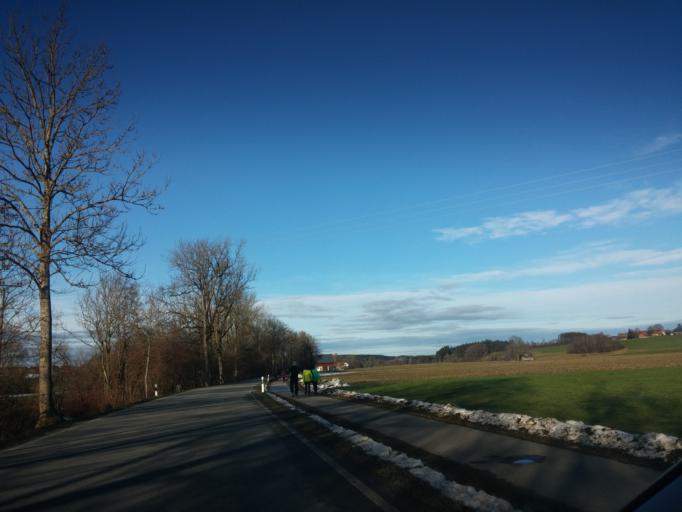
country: DE
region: Bavaria
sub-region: Swabia
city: Legau
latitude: 47.8295
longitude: 10.0970
